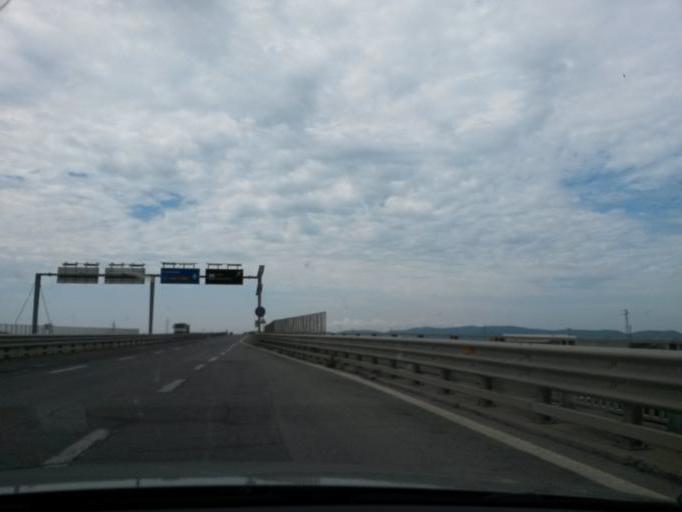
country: IT
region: Tuscany
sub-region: Provincia di Livorno
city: Venturina
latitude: 43.0150
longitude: 10.5973
